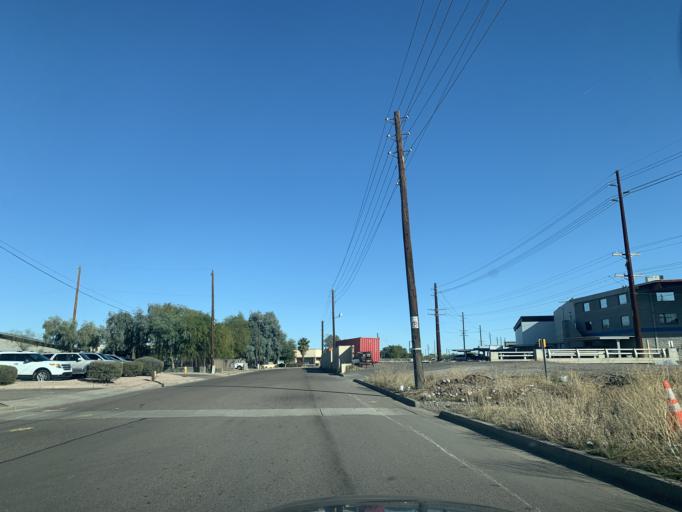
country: US
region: Arizona
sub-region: Maricopa County
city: Tempe Junction
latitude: 33.4169
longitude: -111.9927
